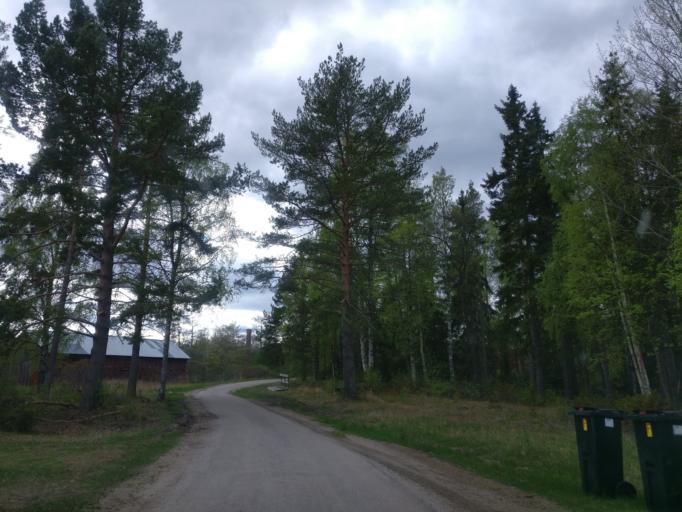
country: SE
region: Gaevleborg
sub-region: Soderhamns Kommun
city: Marielund
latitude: 61.4602
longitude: 17.1336
